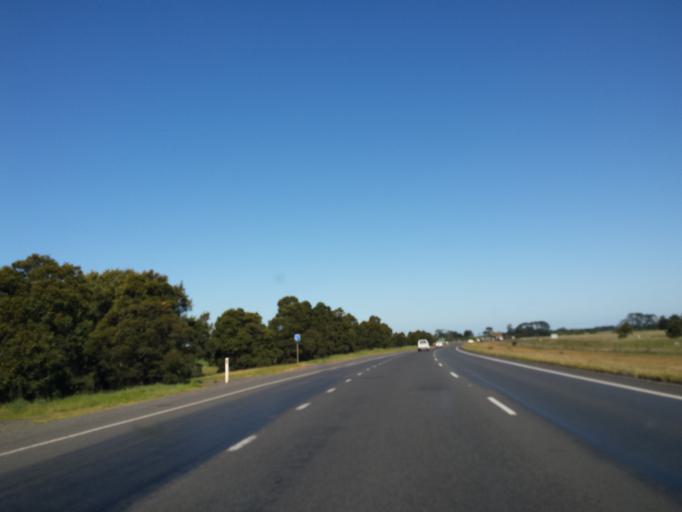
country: AU
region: Victoria
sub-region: Moorabool
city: Bacchus Marsh
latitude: -37.5926
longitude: 144.2475
